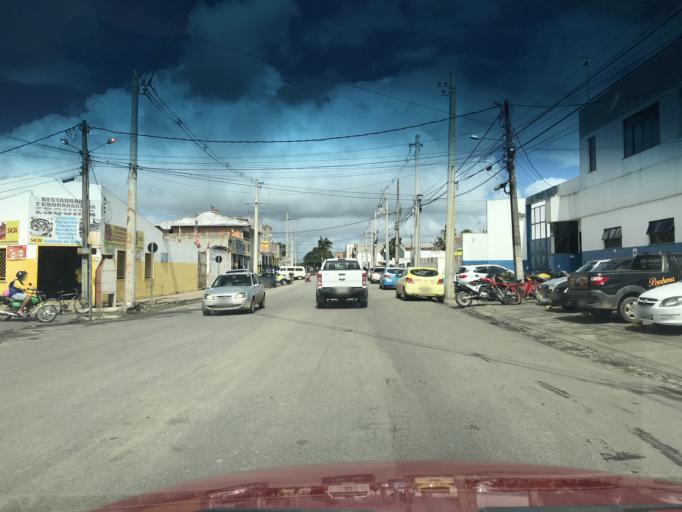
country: BR
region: Bahia
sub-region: Santo Antonio De Jesus
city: Santo Antonio de Jesus
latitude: -12.9674
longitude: -39.2702
